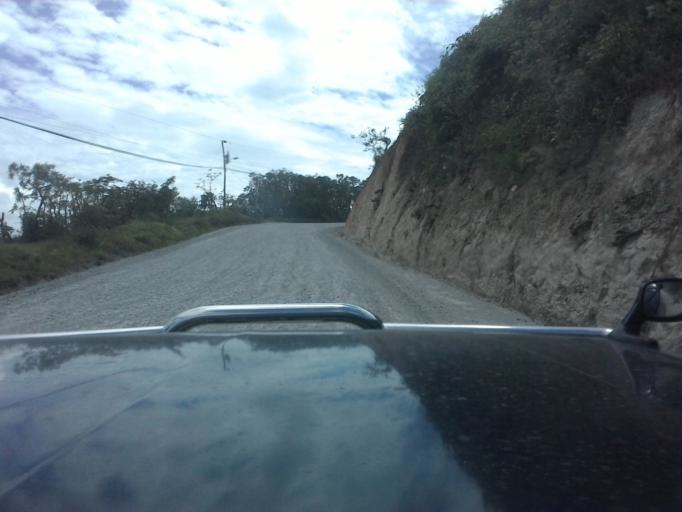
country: CR
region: Guanacaste
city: Juntas
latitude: 10.3006
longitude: -84.8364
